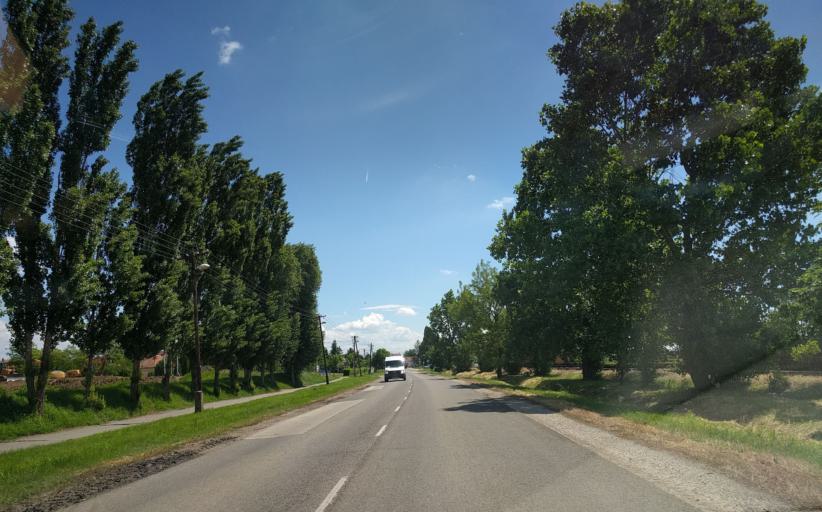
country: HU
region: Jasz-Nagykun-Szolnok
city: Toszeg
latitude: 47.0993
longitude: 20.1368
